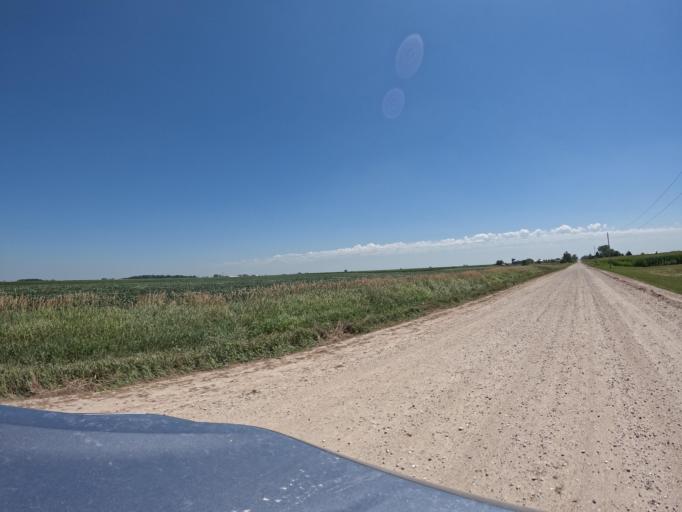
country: US
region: Iowa
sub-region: Poweshiek County
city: Montezuma
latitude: 41.4770
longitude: -92.3936
